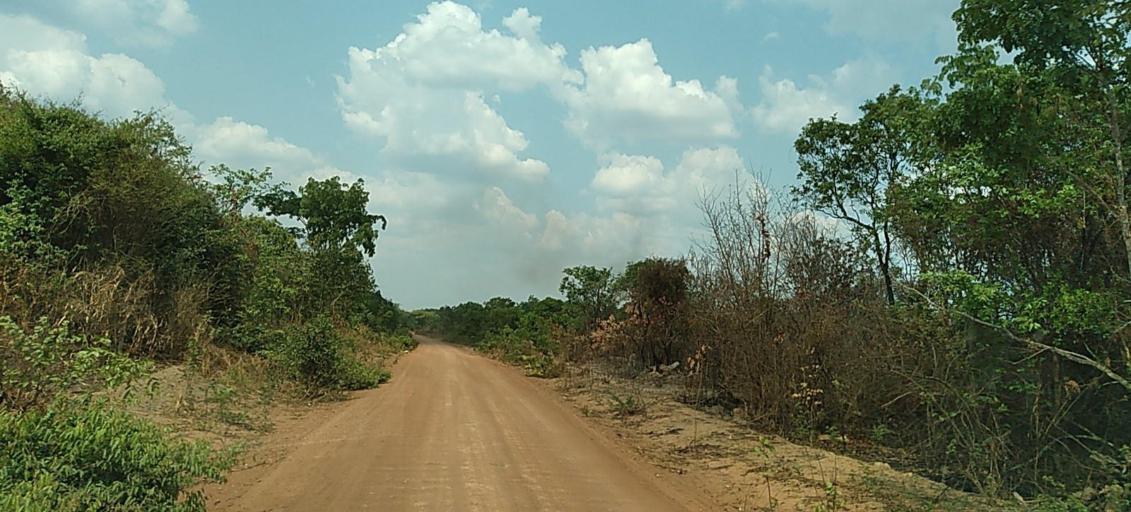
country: ZM
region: Copperbelt
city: Luanshya
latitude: -13.1415
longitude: 28.3292
